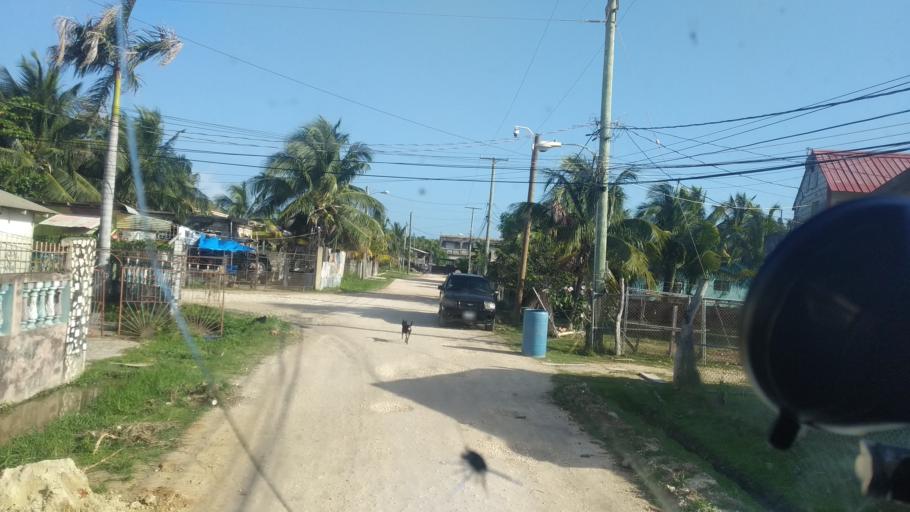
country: BZ
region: Belize
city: Belize City
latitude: 17.4852
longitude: -88.2048
